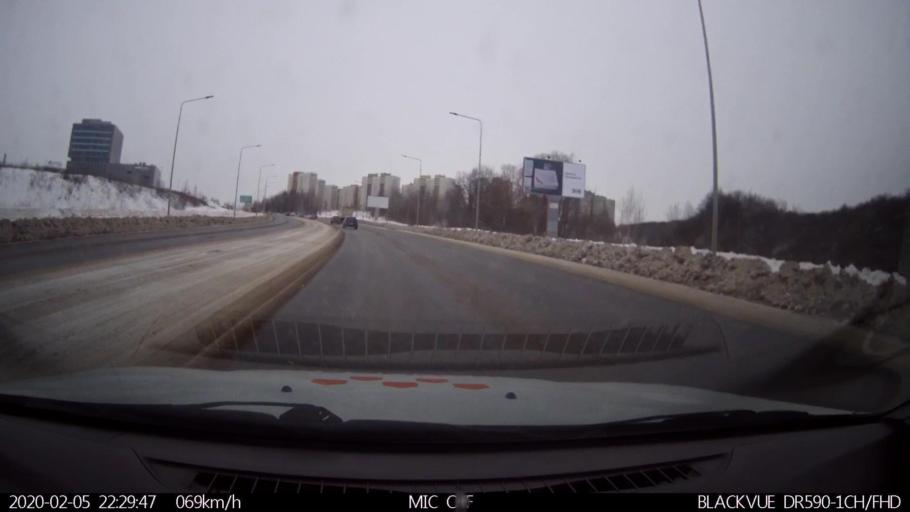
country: RU
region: Nizjnij Novgorod
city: Imeni Stepana Razina
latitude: 54.7468
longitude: 44.1490
